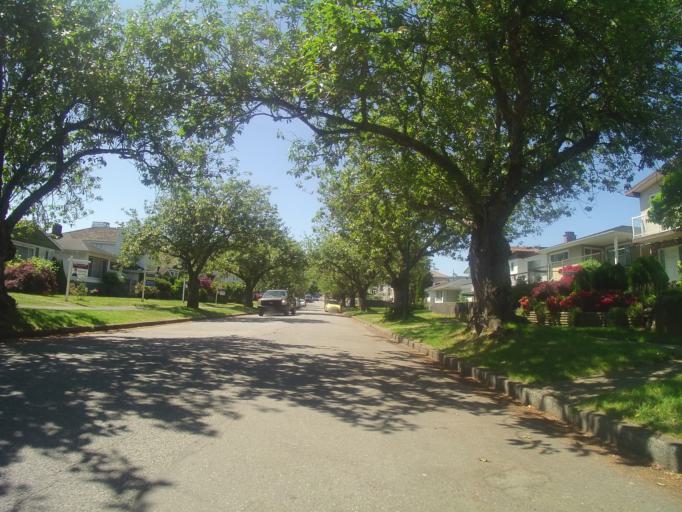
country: CA
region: British Columbia
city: Vancouver
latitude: 49.2134
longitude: -123.1075
